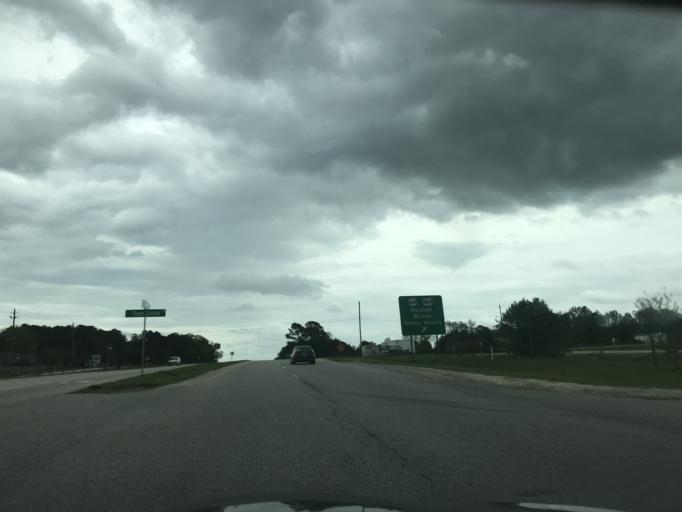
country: US
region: North Carolina
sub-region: Wake County
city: Knightdale
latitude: 35.8043
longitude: -78.4365
